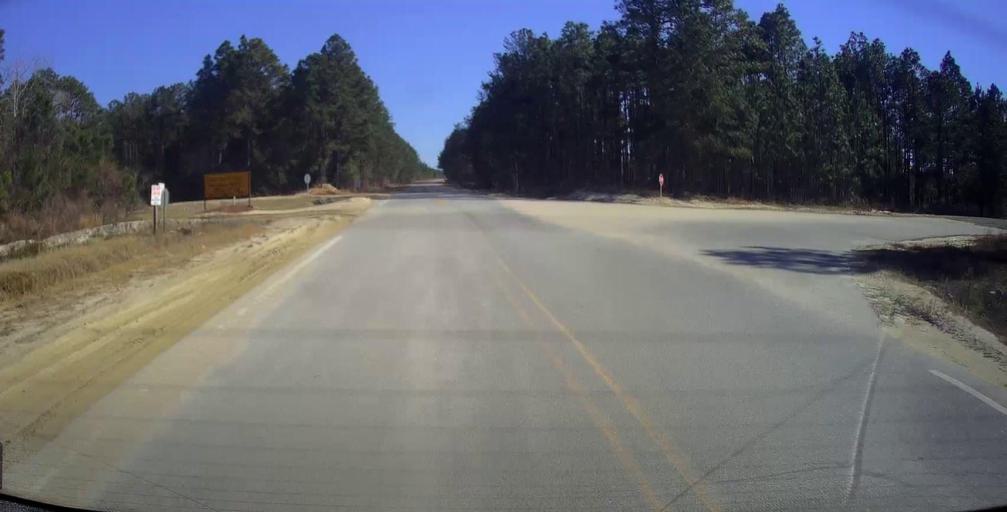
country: US
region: Georgia
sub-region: Crawford County
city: Roberta
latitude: 32.6366
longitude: -83.9980
